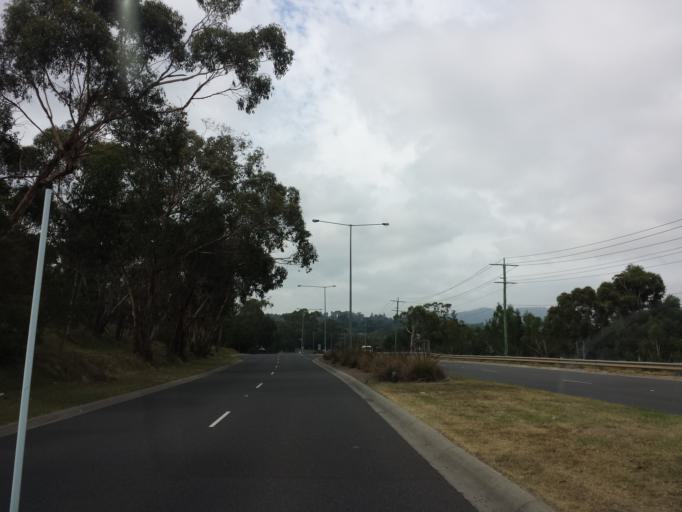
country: AU
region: Victoria
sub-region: Yarra Ranges
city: Lilydale
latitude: -37.7681
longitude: 145.3607
